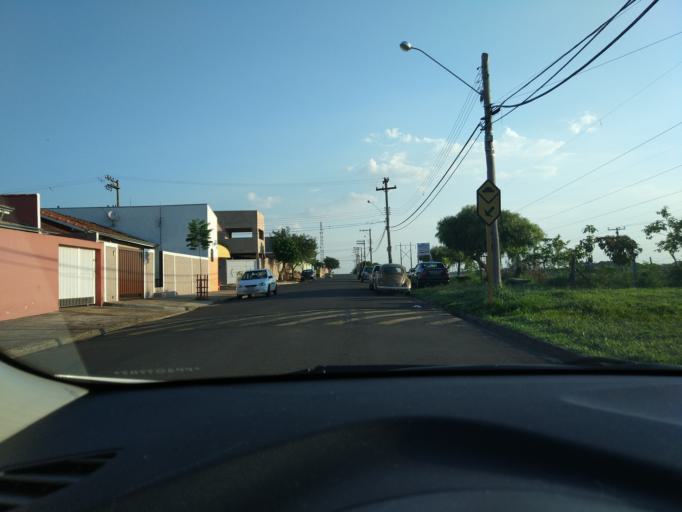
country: BR
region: Sao Paulo
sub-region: Botucatu
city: Botucatu
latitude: -22.9013
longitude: -48.4276
